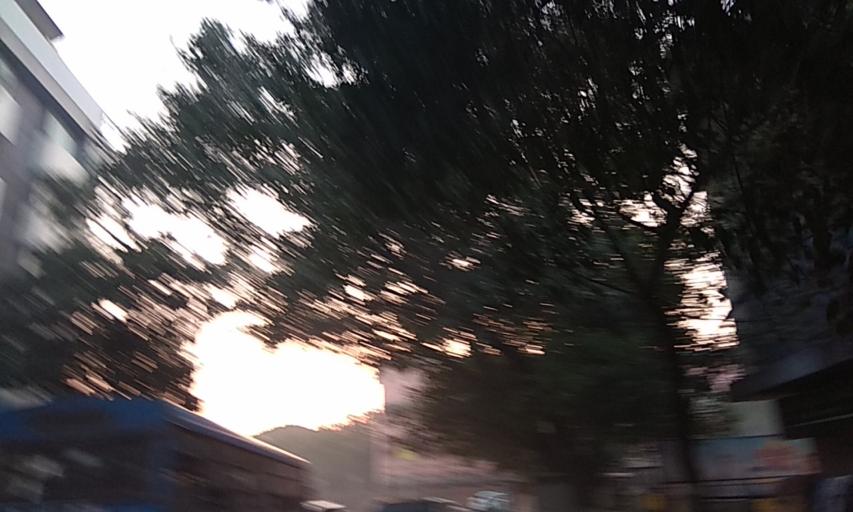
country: IN
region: Maharashtra
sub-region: Pune Division
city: Pune
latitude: 18.5284
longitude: 73.8767
